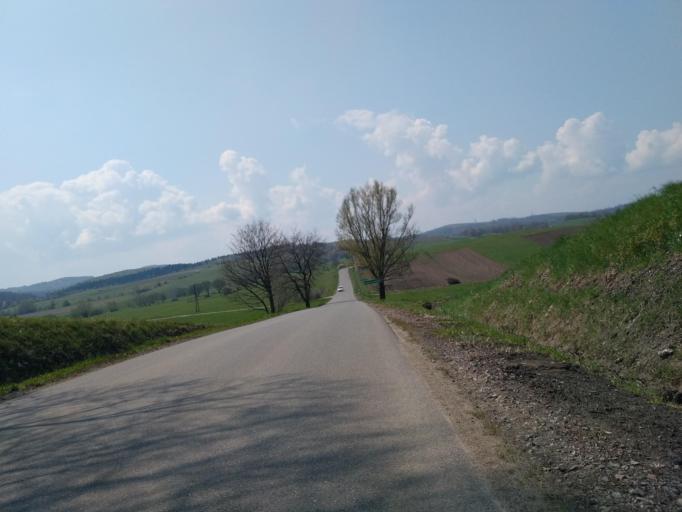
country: PL
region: Subcarpathian Voivodeship
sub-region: Powiat sanocki
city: Zarszyn
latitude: 49.5761
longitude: 22.0096
